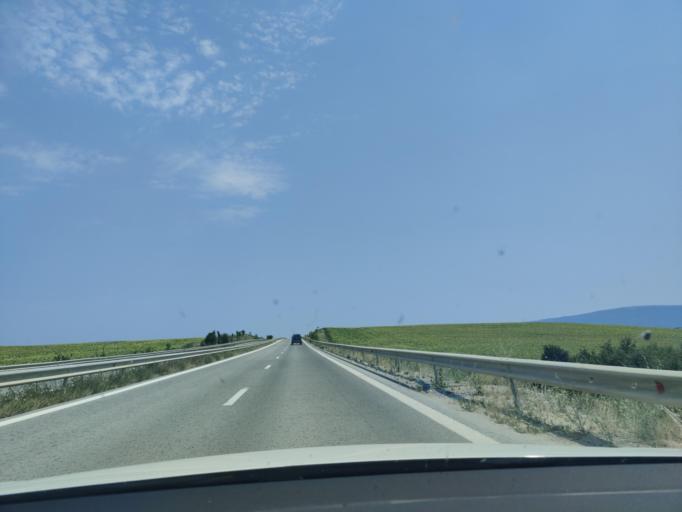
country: BG
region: Montana
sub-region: Obshtina Montana
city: Montana
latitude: 43.4322
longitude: 23.1848
